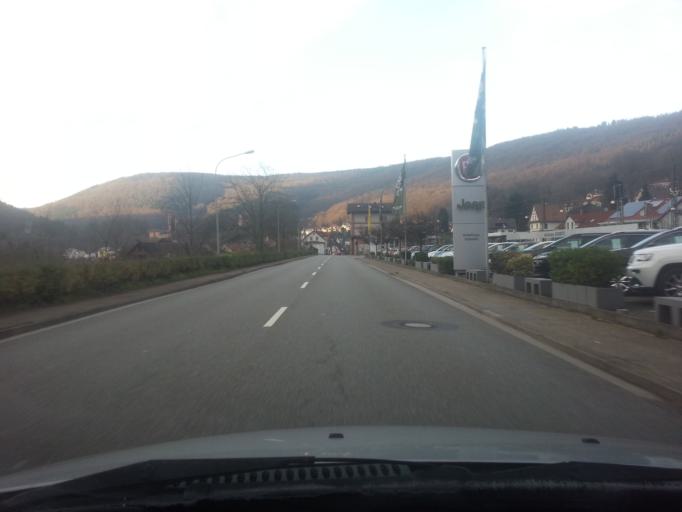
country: DE
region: Hesse
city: Neckarsteinach
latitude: 49.4035
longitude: 8.8422
